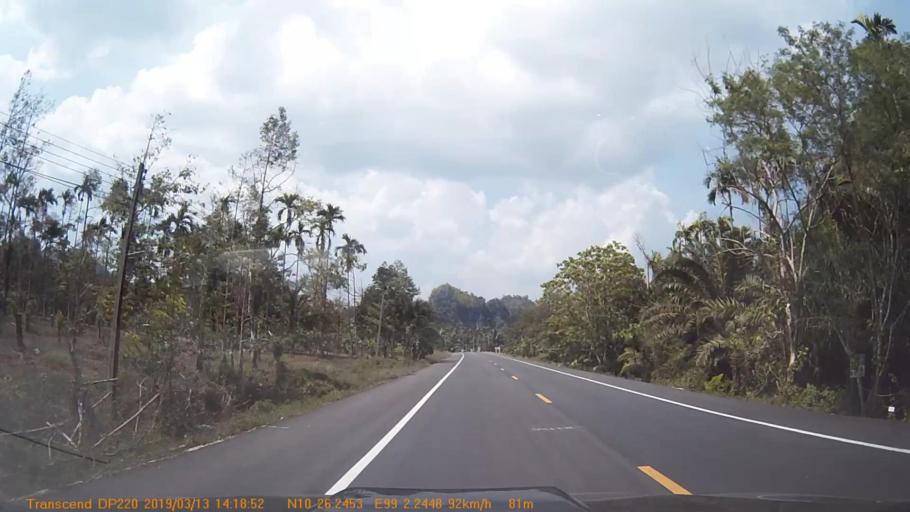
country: TH
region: Chumphon
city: Chumphon
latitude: 10.4260
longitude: 99.0407
